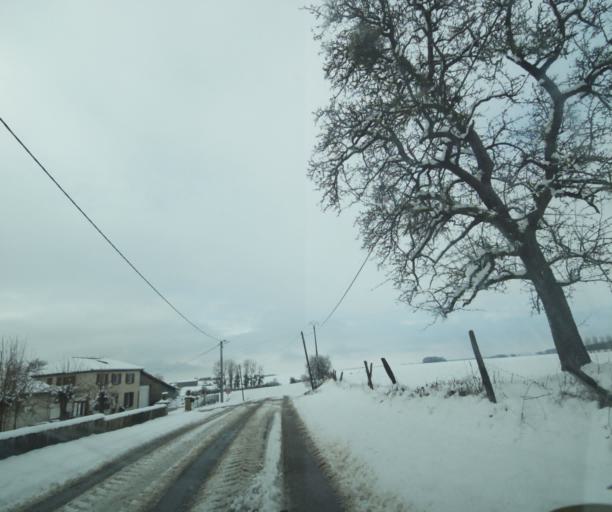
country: FR
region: Champagne-Ardenne
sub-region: Departement de la Haute-Marne
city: Montier-en-Der
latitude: 48.5250
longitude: 4.7091
